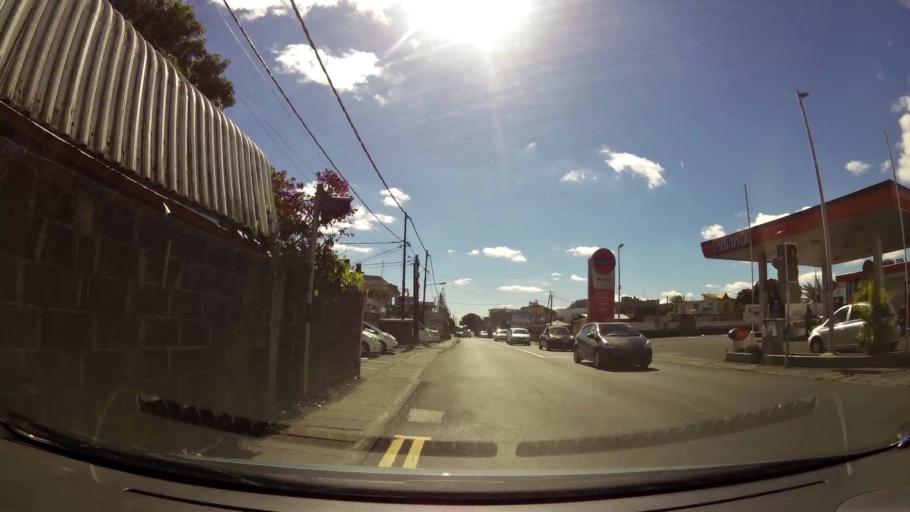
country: MU
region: Plaines Wilhems
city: Vacoas
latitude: -20.2907
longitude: 57.4821
